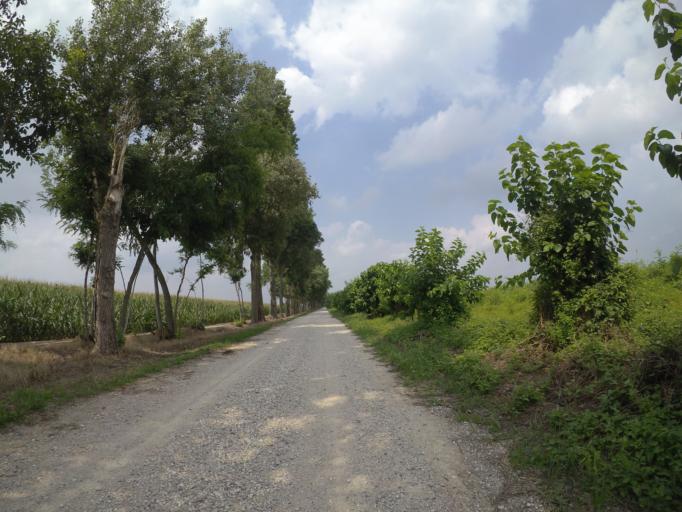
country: IT
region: Friuli Venezia Giulia
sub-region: Provincia di Udine
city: Sedegliano
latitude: 46.0097
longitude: 13.0107
